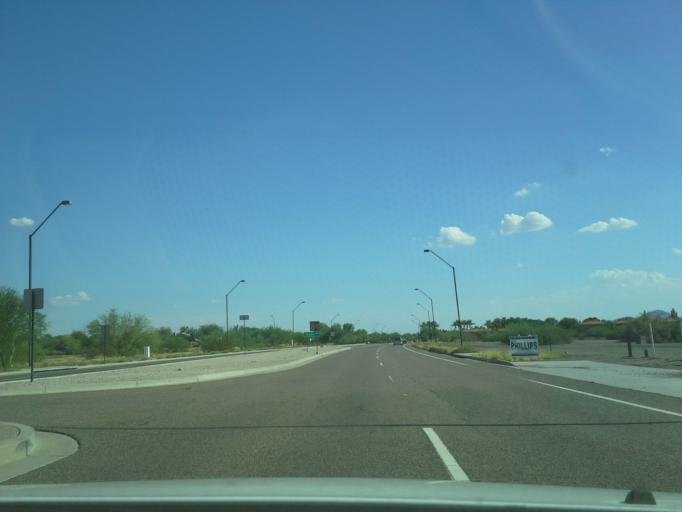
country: US
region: Arizona
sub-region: Maricopa County
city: Paradise Valley
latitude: 33.6517
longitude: -111.9080
